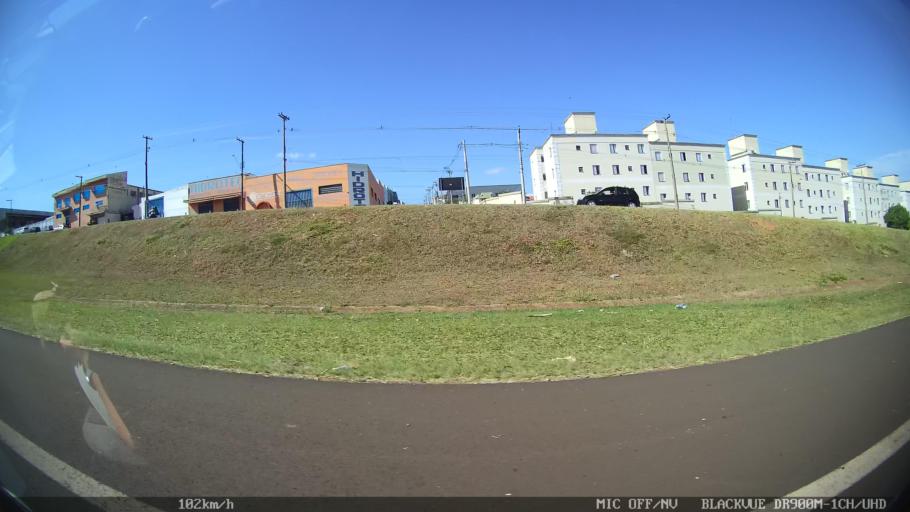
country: BR
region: Sao Paulo
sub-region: Franca
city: Franca
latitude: -20.5162
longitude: -47.4158
